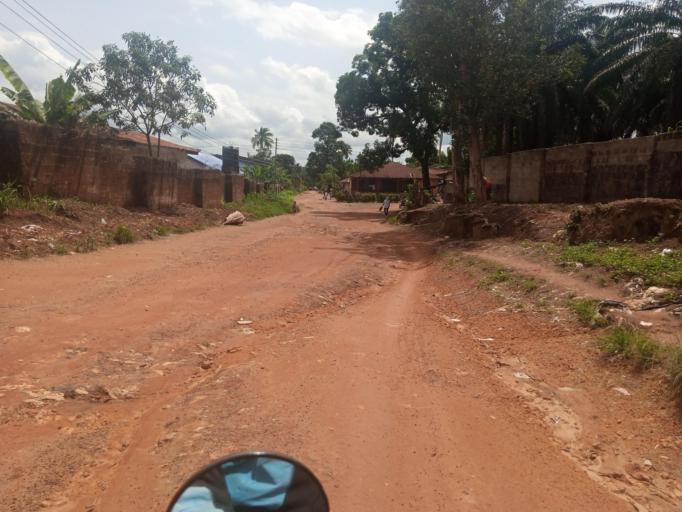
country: SL
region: Southern Province
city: Bo
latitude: 7.9714
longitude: -11.7336
